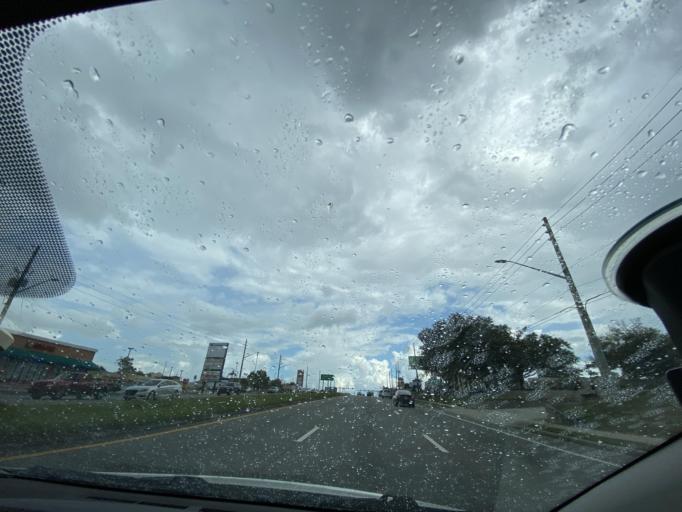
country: US
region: Florida
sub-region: Orange County
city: Orlovista
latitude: 28.5520
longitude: -81.4704
